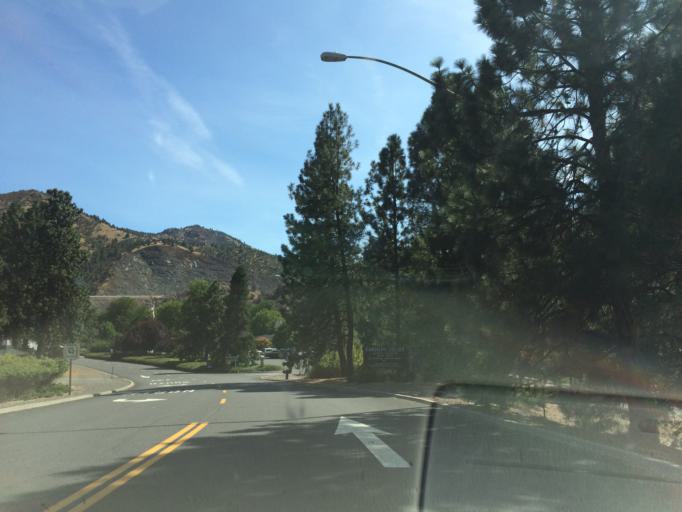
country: US
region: California
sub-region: Siskiyou County
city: Montague
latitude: 41.8547
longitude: -122.5728
